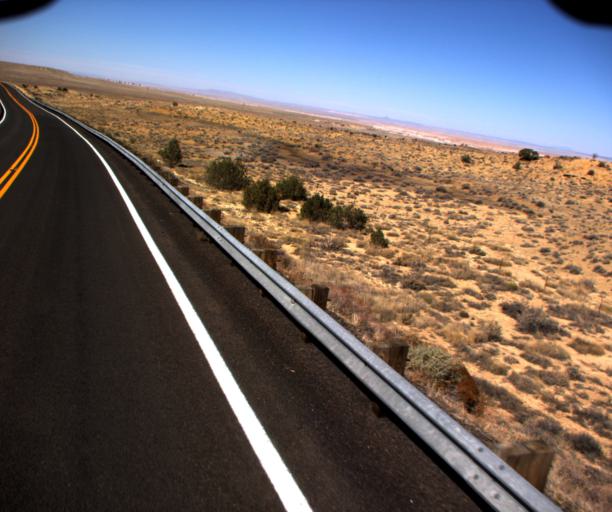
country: US
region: Arizona
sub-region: Coconino County
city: Tuba City
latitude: 35.9292
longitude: -110.8902
